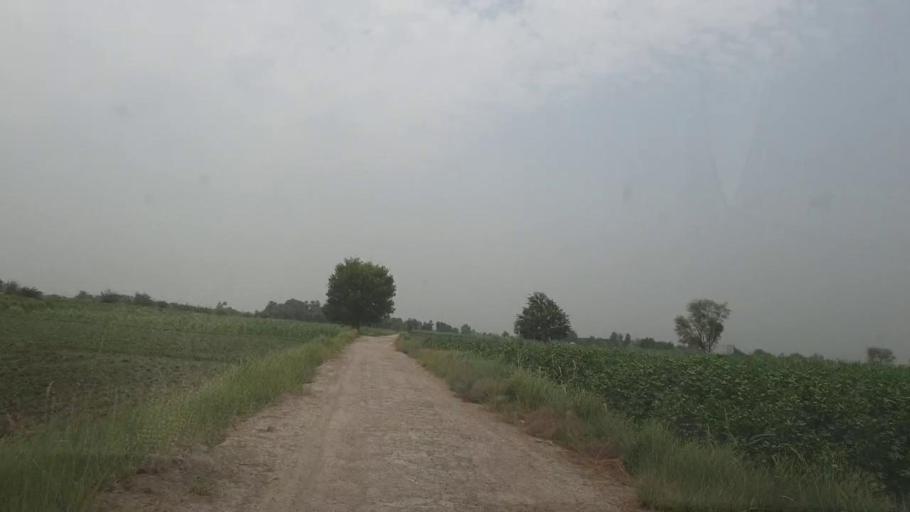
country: PK
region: Sindh
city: Kot Diji
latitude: 27.4273
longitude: 68.6203
